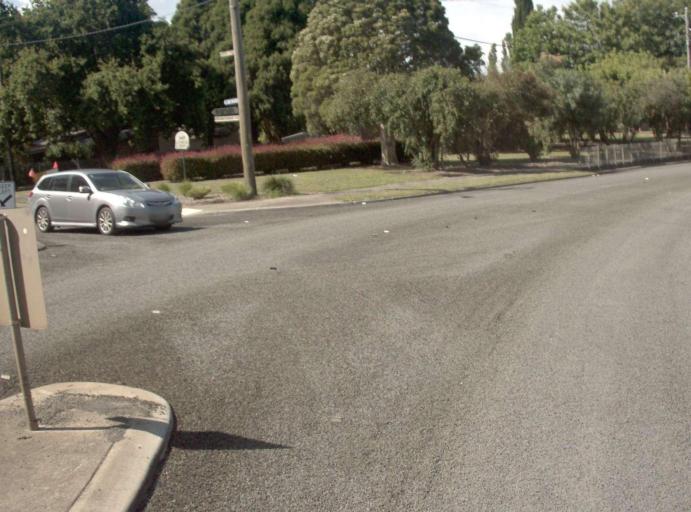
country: AU
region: Victoria
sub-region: Baw Baw
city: Warragul
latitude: -38.1382
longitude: 145.8554
